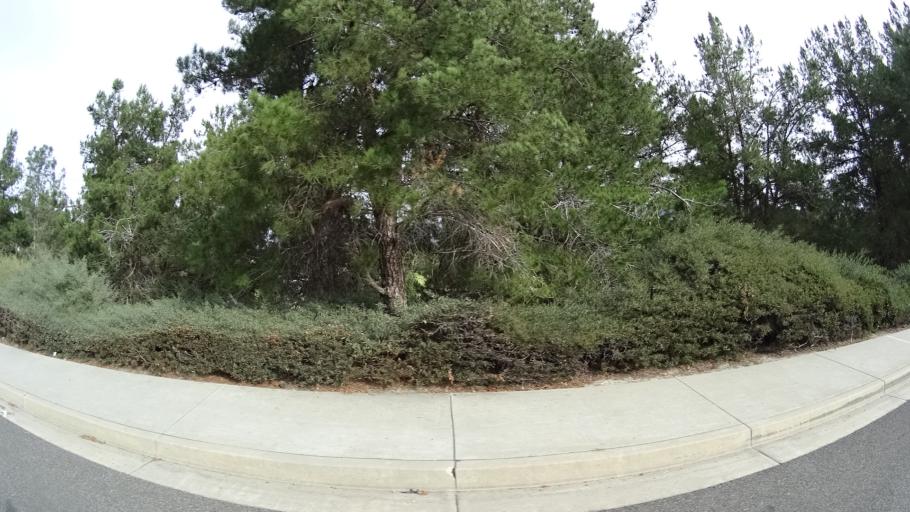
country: US
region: California
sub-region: Orange County
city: Laguna Woods
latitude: 33.5889
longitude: -117.7215
